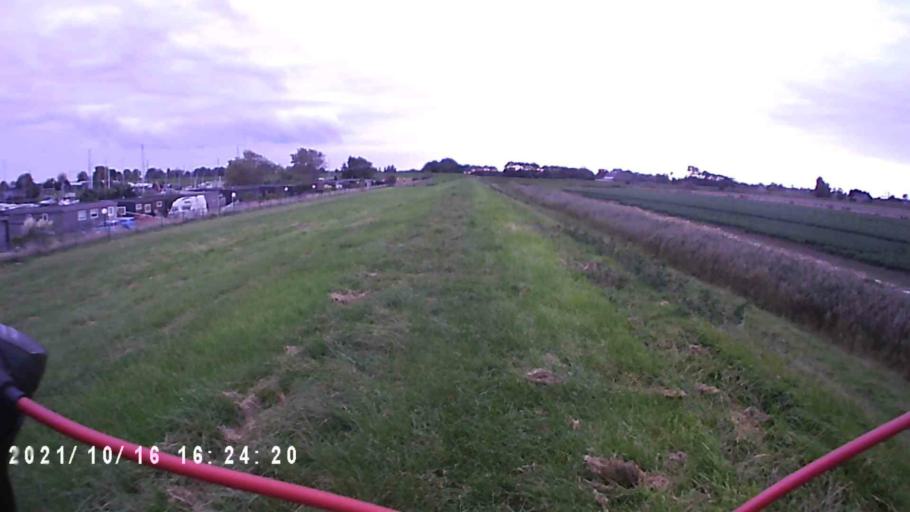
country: NL
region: Friesland
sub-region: Gemeente Dongeradeel
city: Anjum
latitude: 53.3847
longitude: 6.1566
